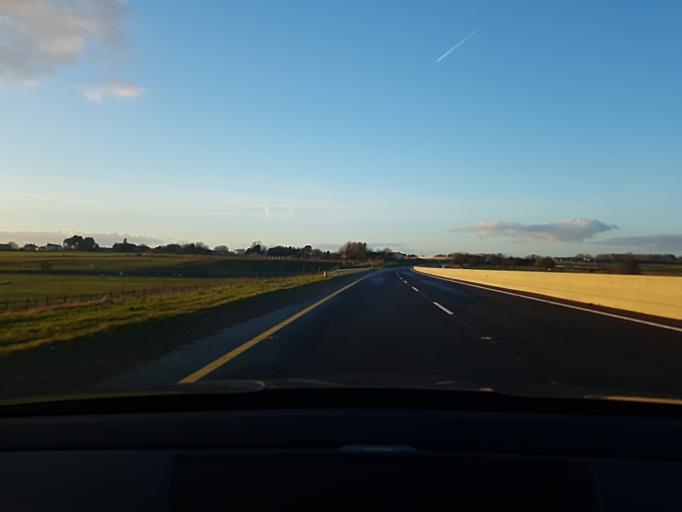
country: IE
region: Connaught
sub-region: County Galway
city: Tuam
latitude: 53.4313
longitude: -8.8405
